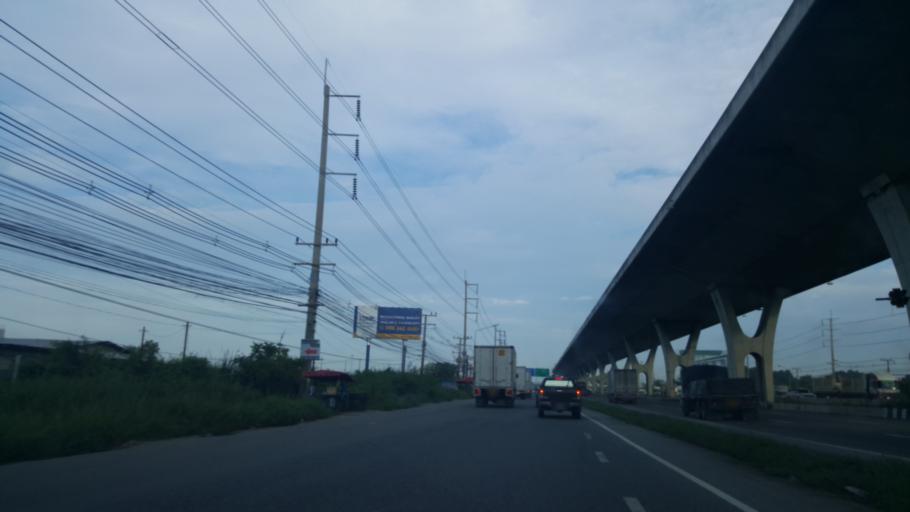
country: TH
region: Chachoengsao
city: Bang Pakong
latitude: 13.5657
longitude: 100.9427
